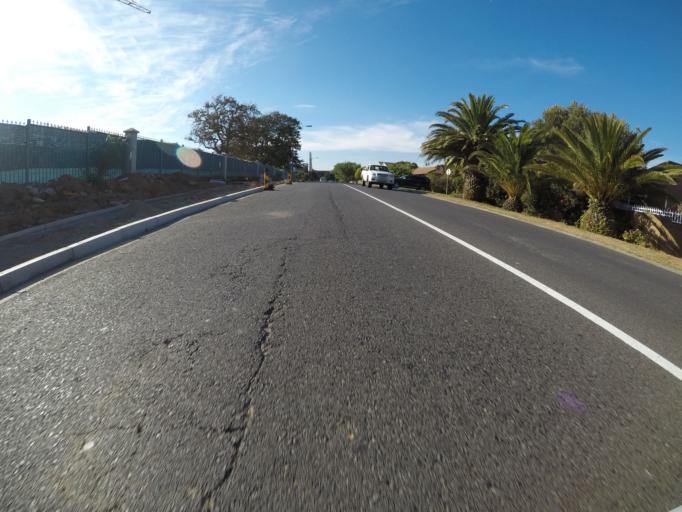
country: ZA
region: Western Cape
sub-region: City of Cape Town
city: Kraaifontein
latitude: -33.8769
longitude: 18.6457
